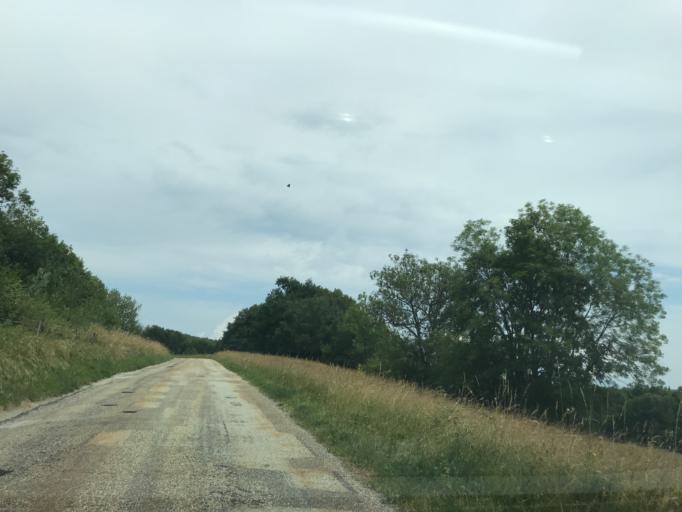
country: FR
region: Rhone-Alpes
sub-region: Departement de l'Isere
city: Barraux
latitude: 45.4226
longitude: 5.9608
